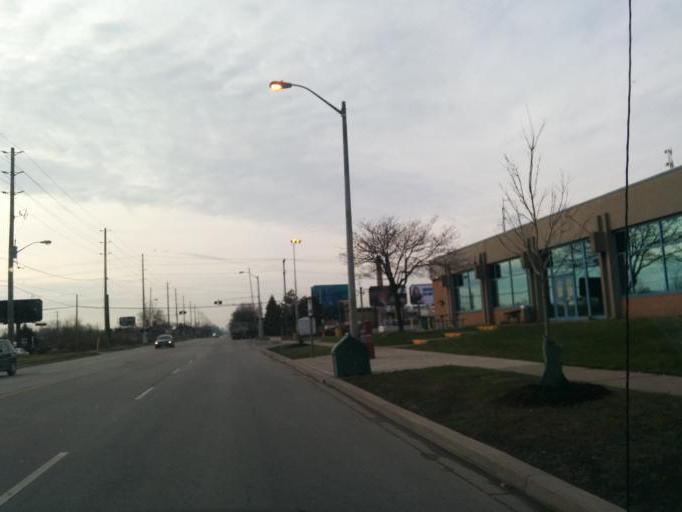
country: CA
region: Ontario
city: Etobicoke
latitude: 43.6154
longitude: -79.5281
